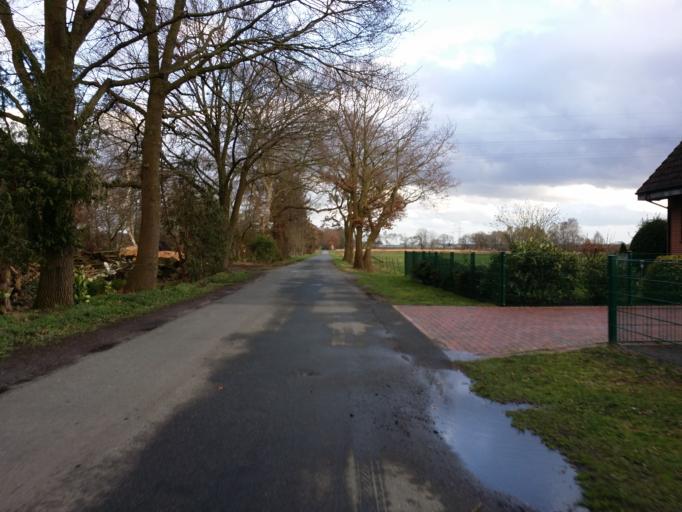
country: DE
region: Lower Saxony
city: Delmenhorst
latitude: 53.0202
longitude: 8.6285
